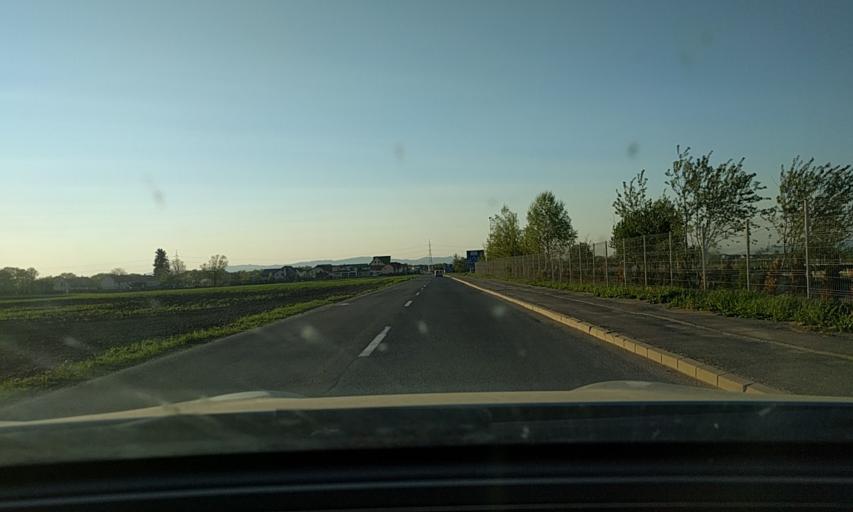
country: RO
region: Brasov
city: Brasov
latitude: 45.6831
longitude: 25.5715
